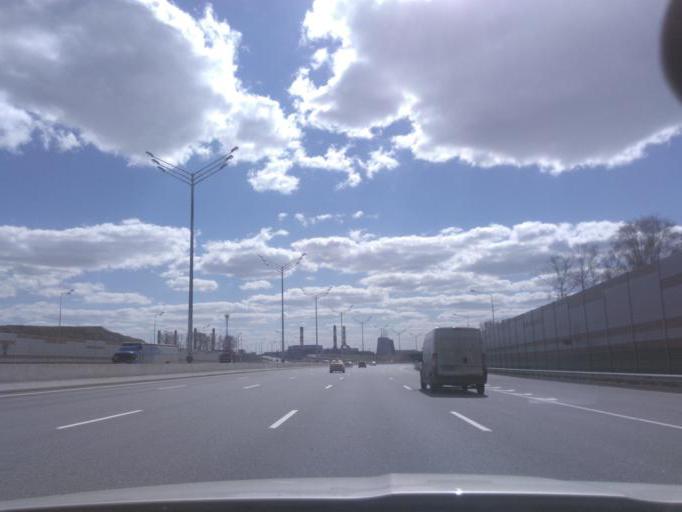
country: RU
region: Moskovskaya
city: Levoberezhnaya
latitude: 55.9042
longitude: 37.4807
